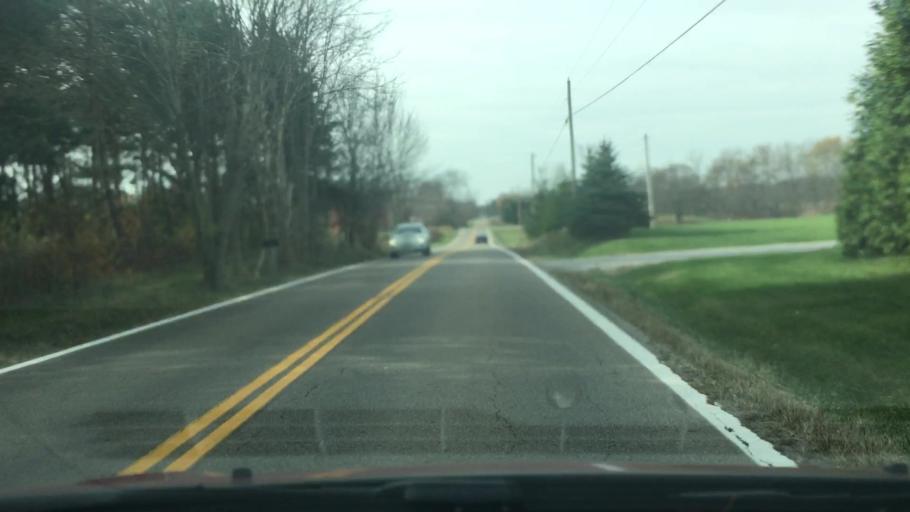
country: US
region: Ohio
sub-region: Delaware County
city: Sunbury
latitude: 40.3325
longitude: -82.8067
